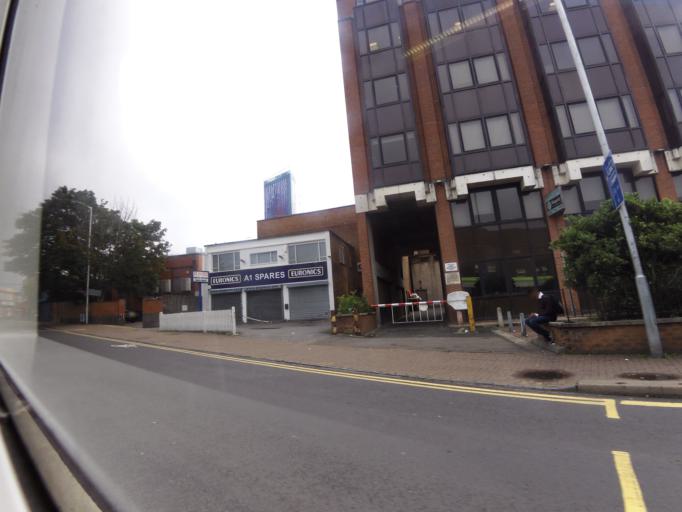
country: GB
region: England
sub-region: Greater London
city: Croydon
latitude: 51.3764
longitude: -0.1029
